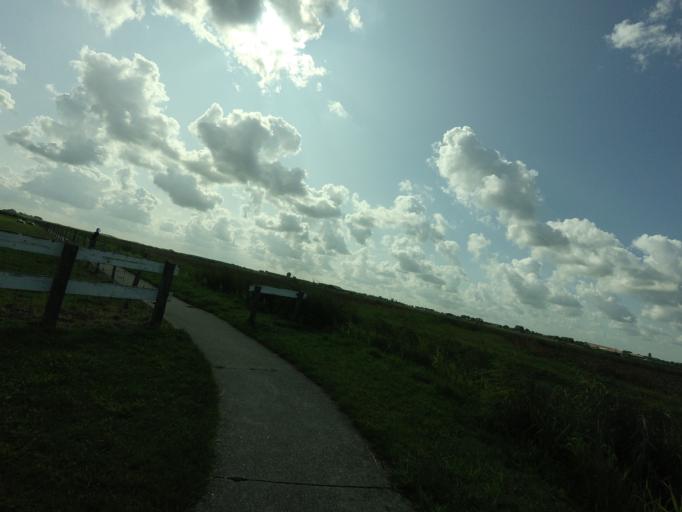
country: NL
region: Friesland
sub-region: Gemeente Het Bildt
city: Sint Jacobiparochie
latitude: 53.2683
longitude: 5.6092
